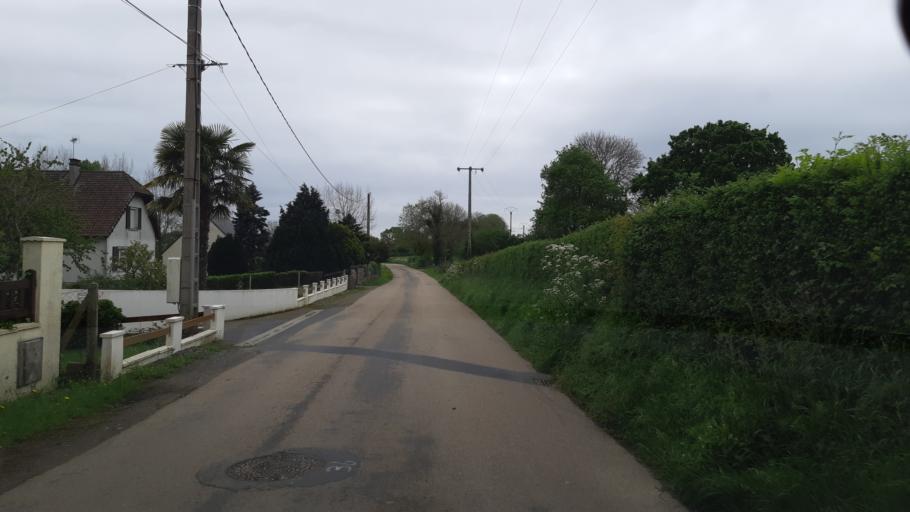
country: FR
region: Lower Normandy
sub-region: Departement de la Manche
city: Donville-les-Bains
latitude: 48.8589
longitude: -1.5453
